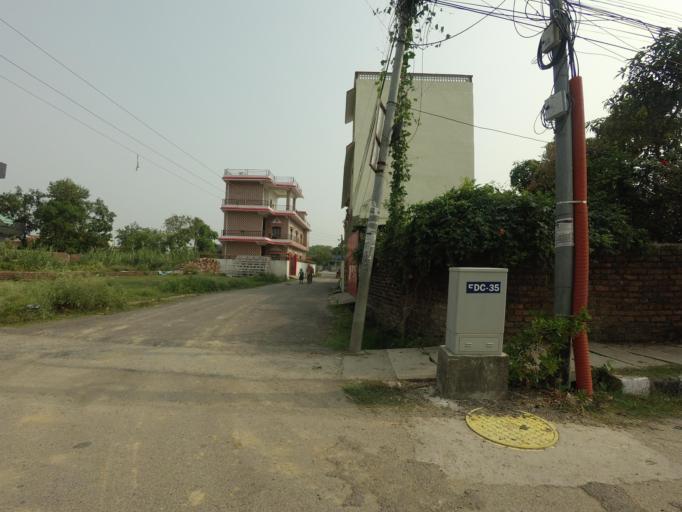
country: NP
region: Western Region
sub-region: Lumbini Zone
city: Bhairahawa
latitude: 27.5182
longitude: 83.4605
